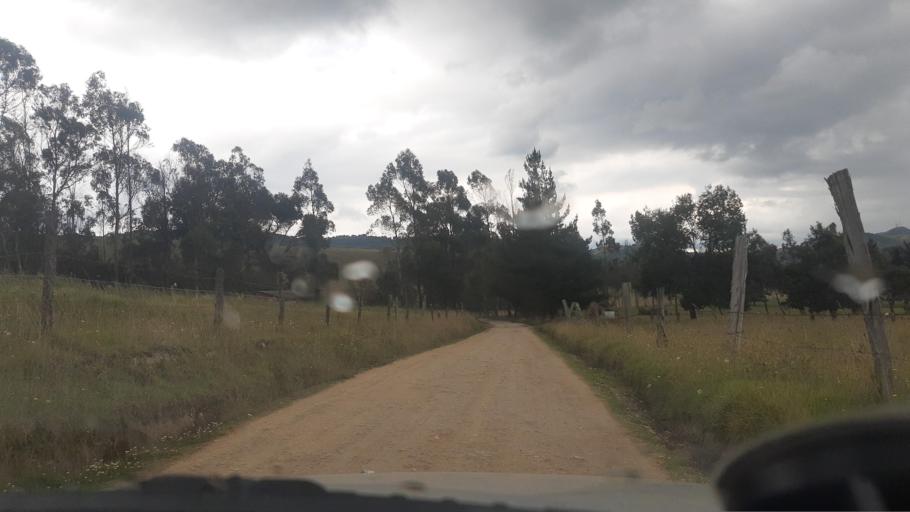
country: CO
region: Cundinamarca
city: Suesca
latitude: 5.1706
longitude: -73.8026
